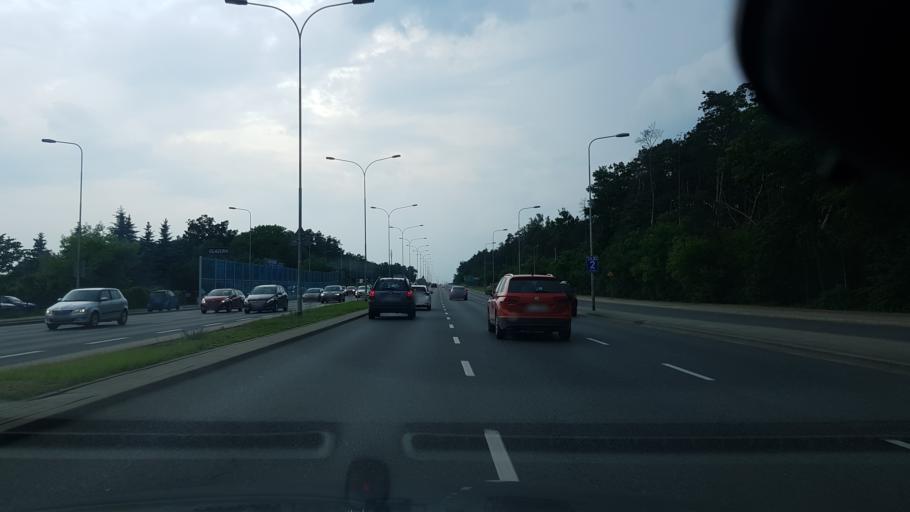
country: PL
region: Masovian Voivodeship
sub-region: Powiat legionowski
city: Jablonna
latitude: 52.3566
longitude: 20.9408
